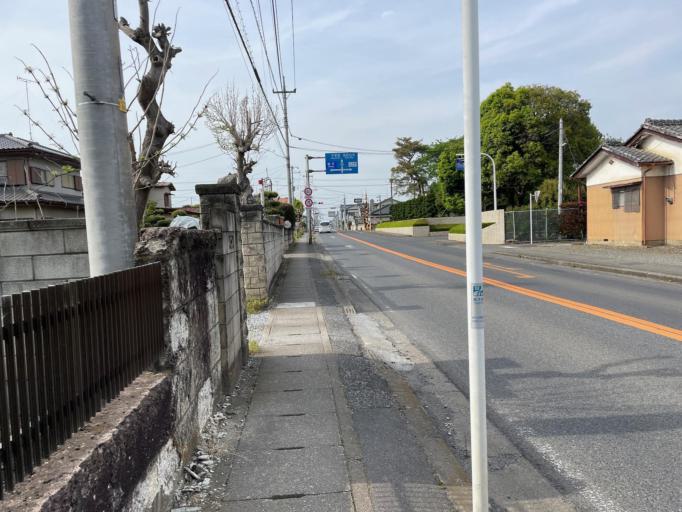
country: JP
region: Tochigi
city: Mibu
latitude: 36.4193
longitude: 139.8026
